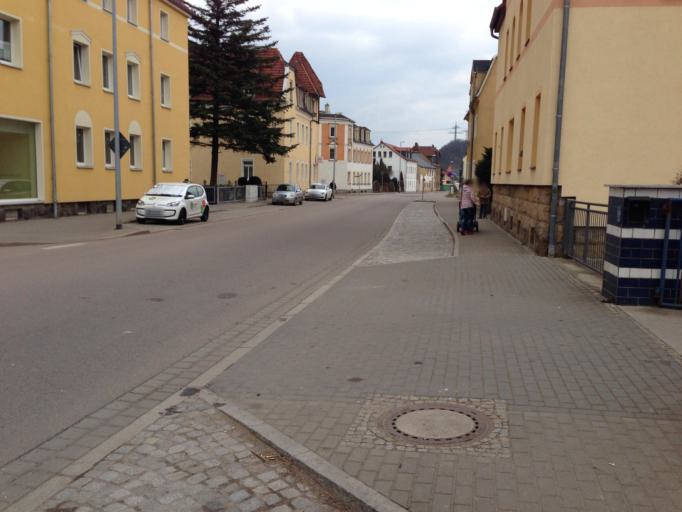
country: DE
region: Saxony
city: Freital
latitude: 51.0122
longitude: 13.6679
